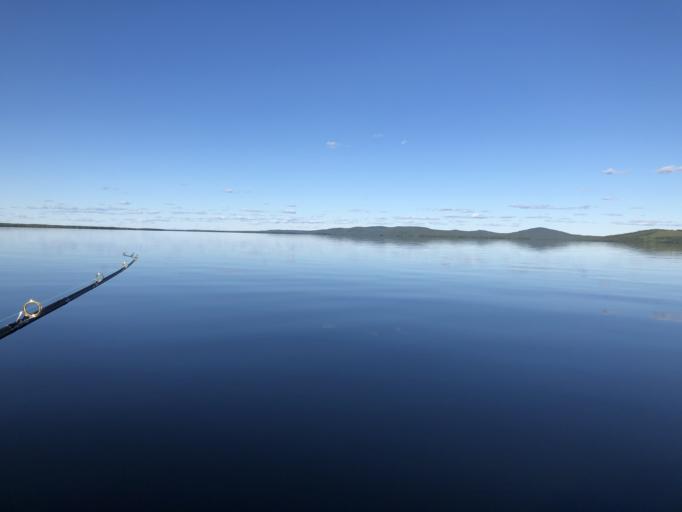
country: FI
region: Lapland
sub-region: Itae-Lappi
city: Posio
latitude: 66.1168
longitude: 28.5878
